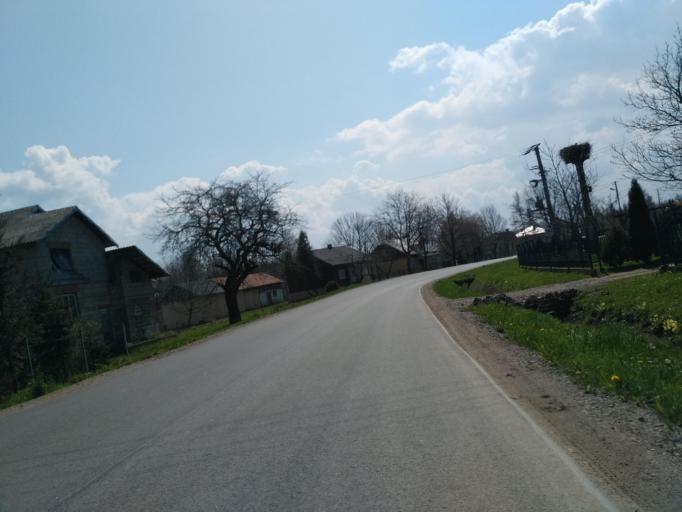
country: PL
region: Subcarpathian Voivodeship
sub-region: Powiat sanocki
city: Zarszyn
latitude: 49.5204
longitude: 21.9994
